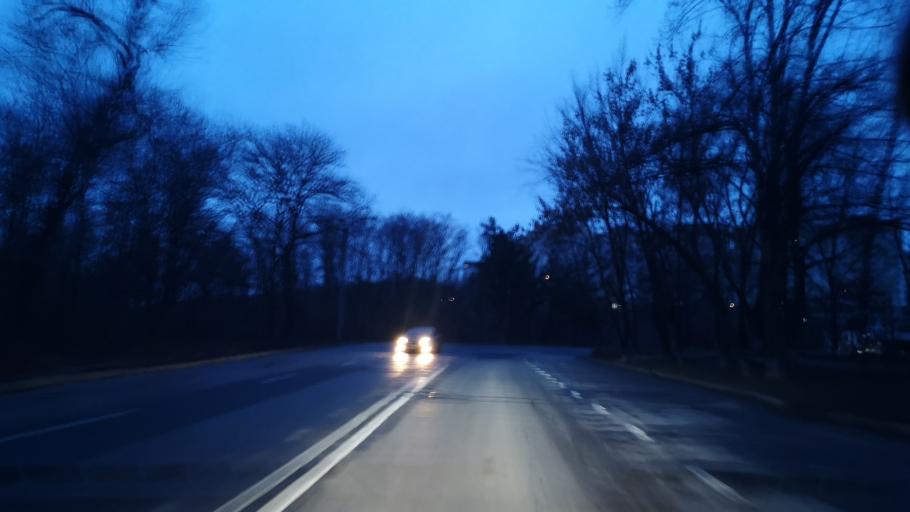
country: MD
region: Chisinau
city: Chisinau
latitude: 47.0388
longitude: 28.8793
